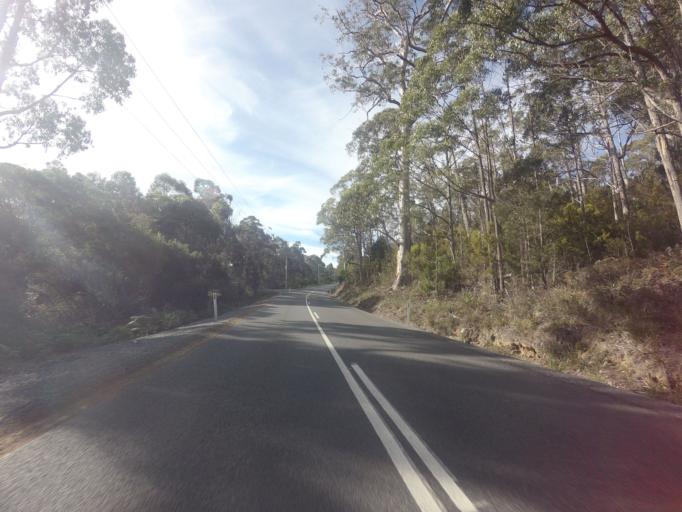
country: AU
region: Tasmania
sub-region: Clarence
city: Sandford
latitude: -43.0598
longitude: 147.8443
